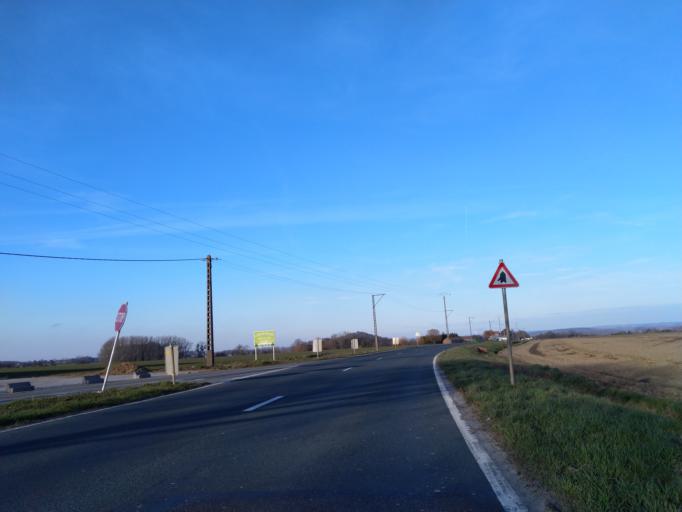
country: BE
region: Wallonia
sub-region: Province du Hainaut
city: Frameries
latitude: 50.3793
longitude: 3.8990
